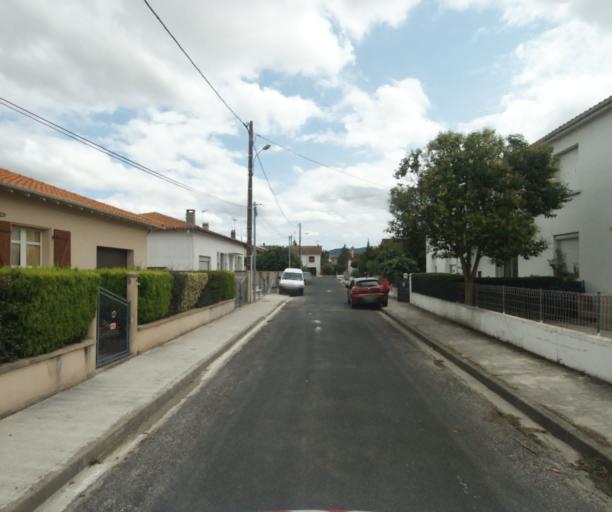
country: FR
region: Midi-Pyrenees
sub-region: Departement de la Haute-Garonne
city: Revel
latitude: 43.4591
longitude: 1.9995
